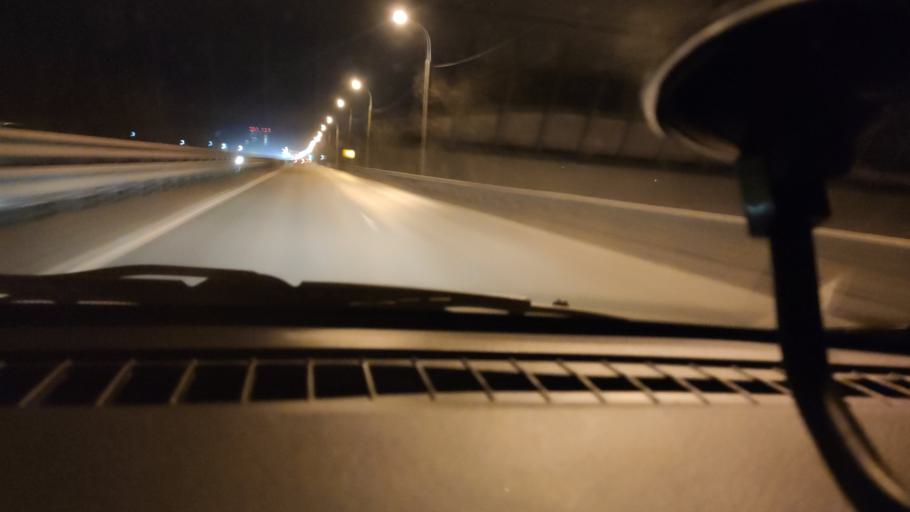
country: RU
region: Samara
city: Samara
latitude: 53.1052
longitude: 50.1614
